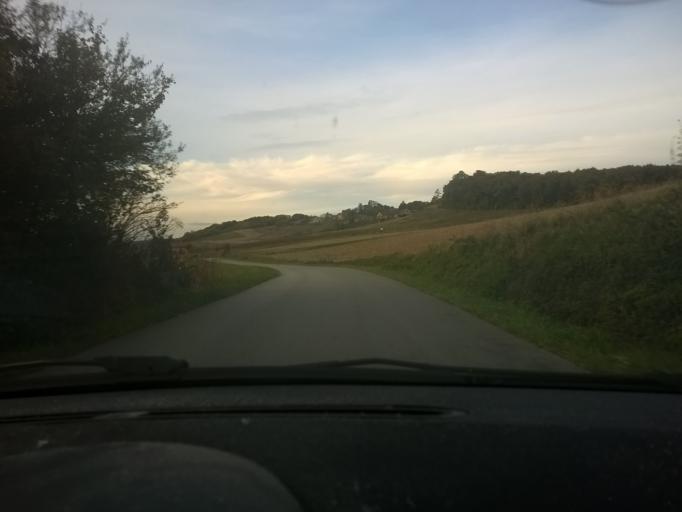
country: HR
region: Krapinsko-Zagorska
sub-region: Grad Krapina
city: Krapina
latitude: 46.1093
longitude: 15.8696
